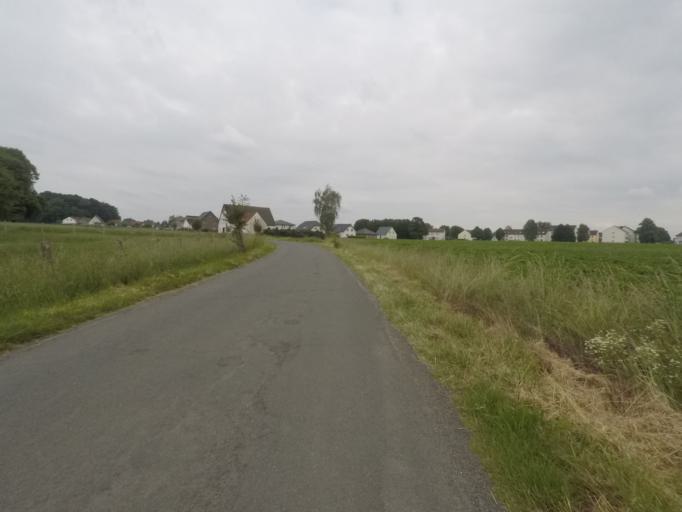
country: DE
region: North Rhine-Westphalia
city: Enger
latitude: 52.1601
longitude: 8.5769
